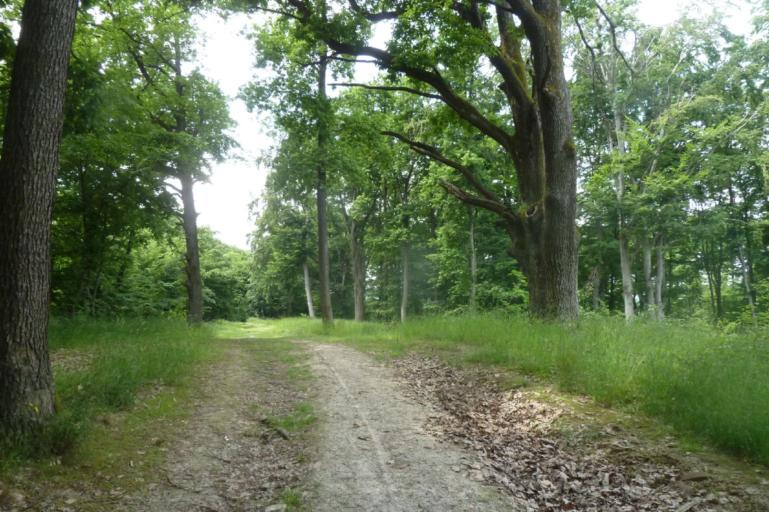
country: HU
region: Pest
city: Csobanka
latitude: 47.6977
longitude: 18.9671
